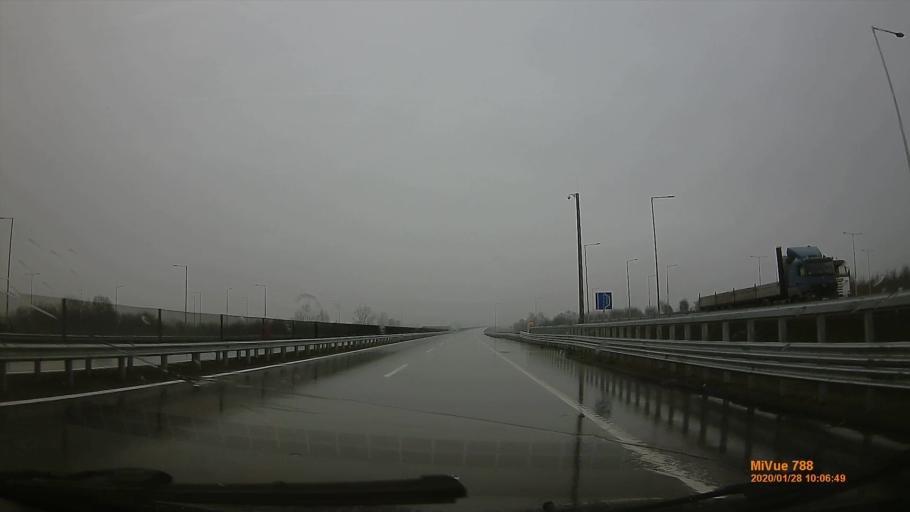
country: HU
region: Pest
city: Pilis
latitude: 47.2876
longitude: 19.5814
